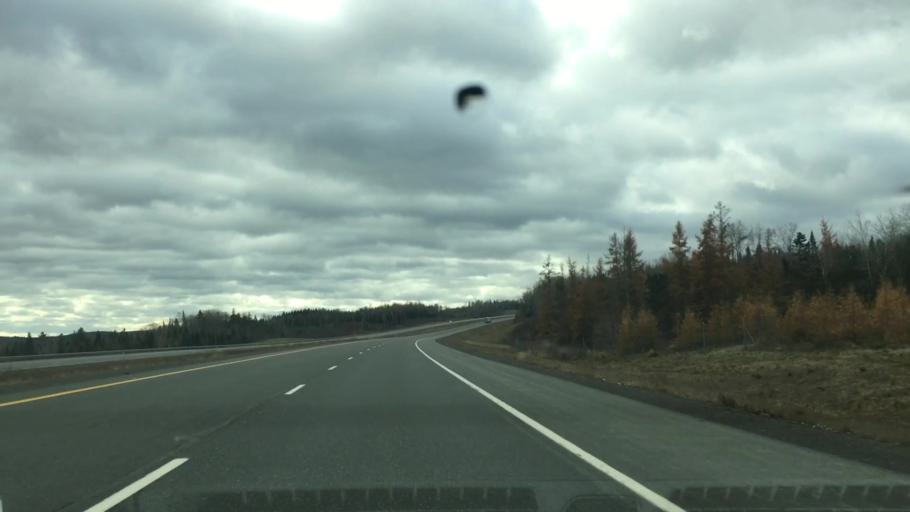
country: US
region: Maine
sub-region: Aroostook County
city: Fort Fairfield
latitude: 46.6704
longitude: -67.7301
